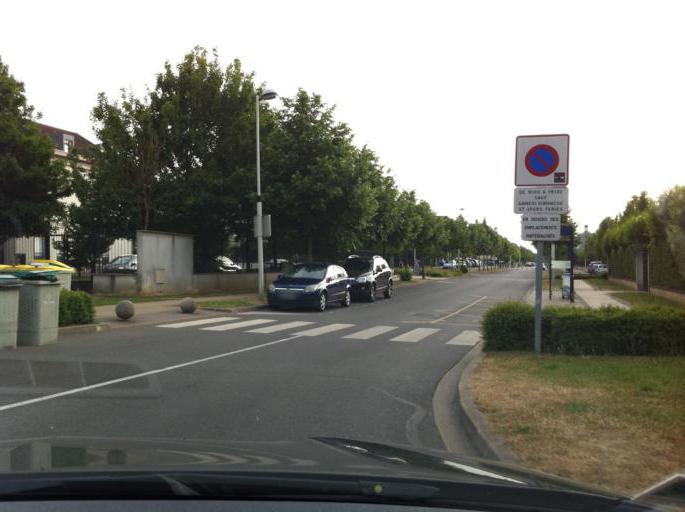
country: FR
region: Ile-de-France
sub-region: Departement de Seine-et-Marne
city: Moissy-Cramayel
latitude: 48.6291
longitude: 2.5803
